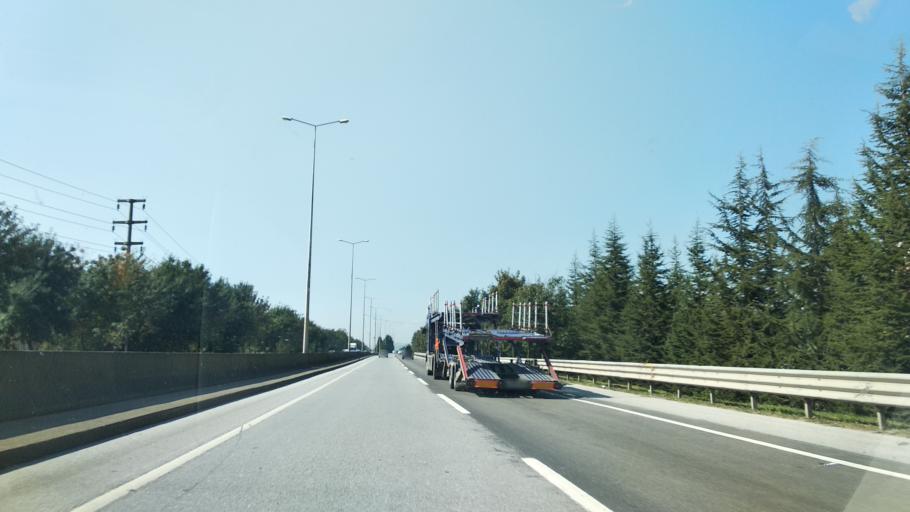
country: TR
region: Kocaeli
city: Kosekoy
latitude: 40.7546
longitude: 30.0155
